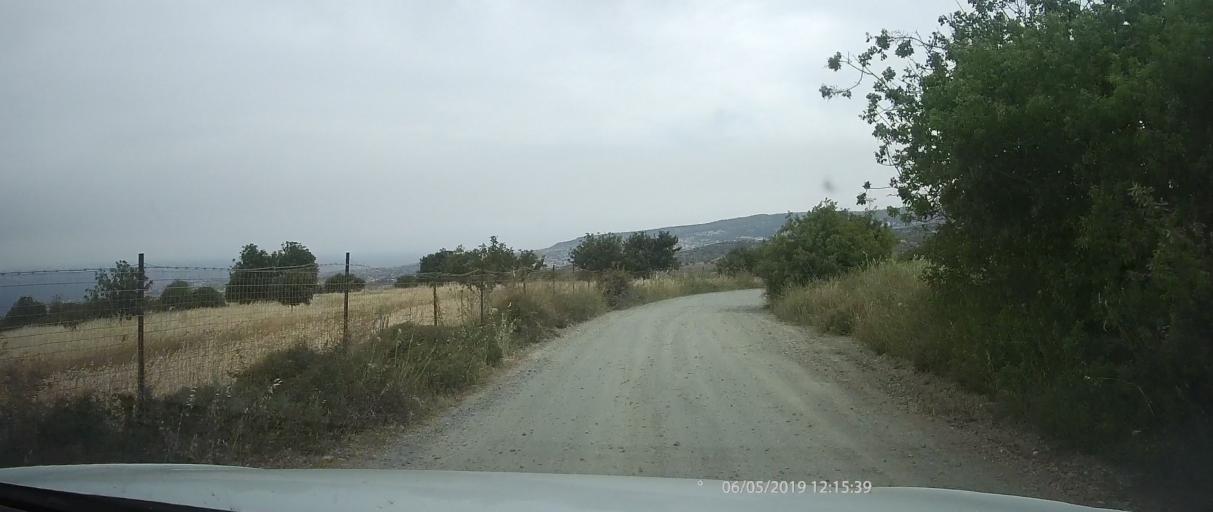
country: CY
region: Pafos
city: Tala
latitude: 34.8521
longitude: 32.4204
